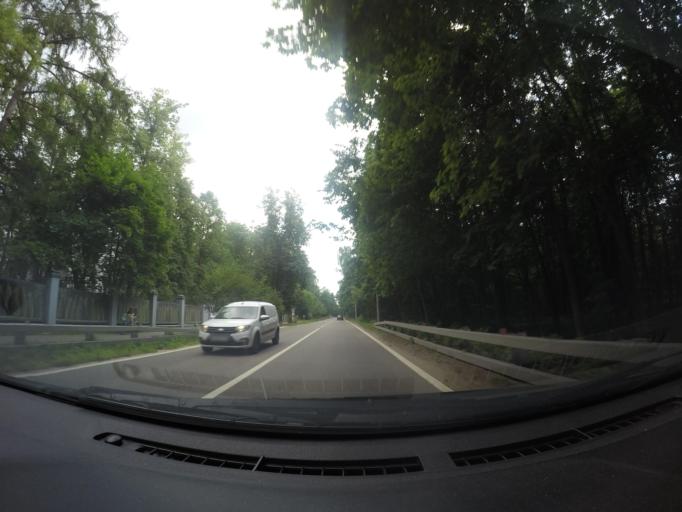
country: RU
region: Moscow
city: Sokol'niki
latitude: 55.8144
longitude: 37.6739
